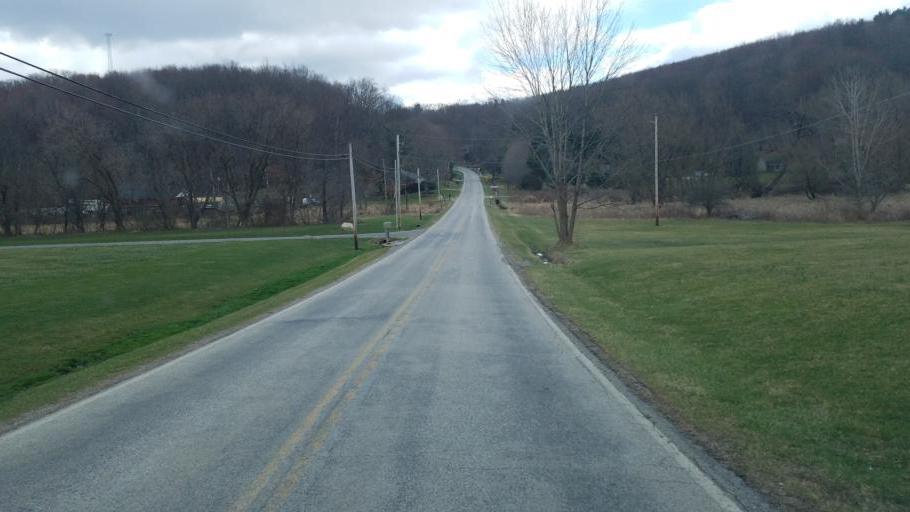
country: US
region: Ohio
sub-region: Sandusky County
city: Bellville
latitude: 40.6241
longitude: -82.5002
